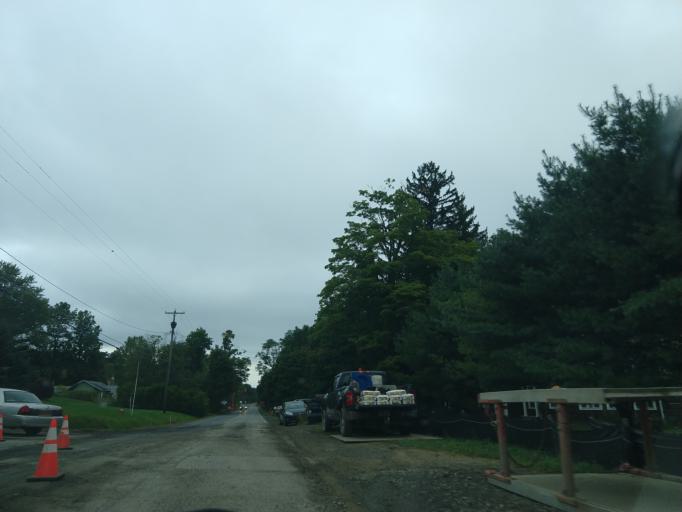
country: US
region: New York
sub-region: Tompkins County
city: East Ithaca
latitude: 42.4039
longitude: -76.4642
